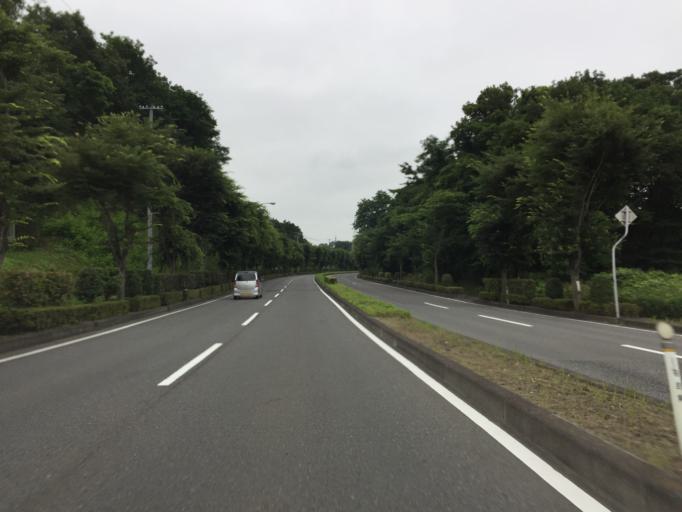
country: JP
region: Fukushima
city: Sukagawa
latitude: 37.2826
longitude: 140.3588
